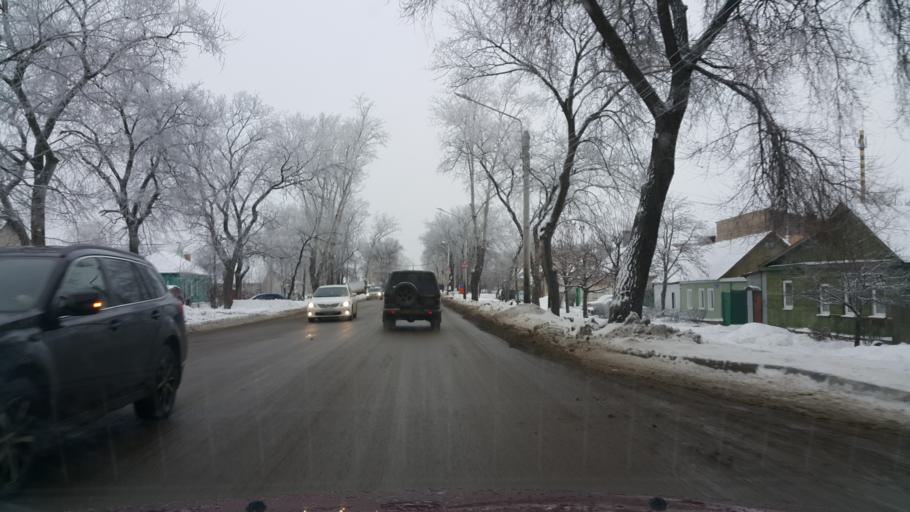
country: RU
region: Tambov
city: Pokrovo-Prigorodnoye
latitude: 52.7003
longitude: 41.4331
